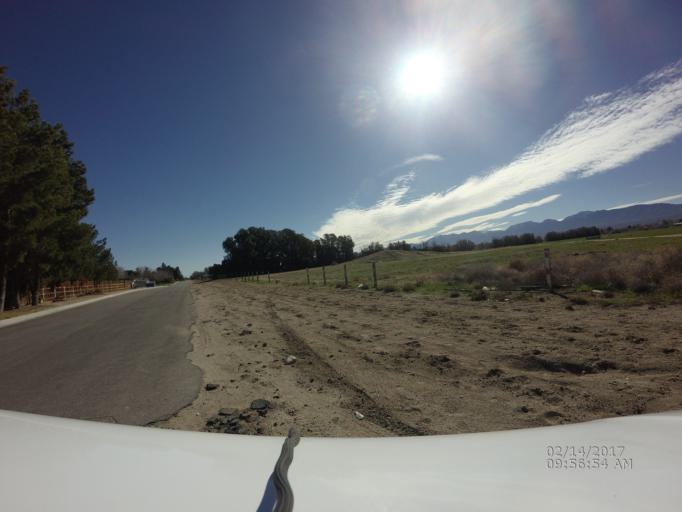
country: US
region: California
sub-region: Los Angeles County
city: Littlerock
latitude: 34.5502
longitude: -117.9614
